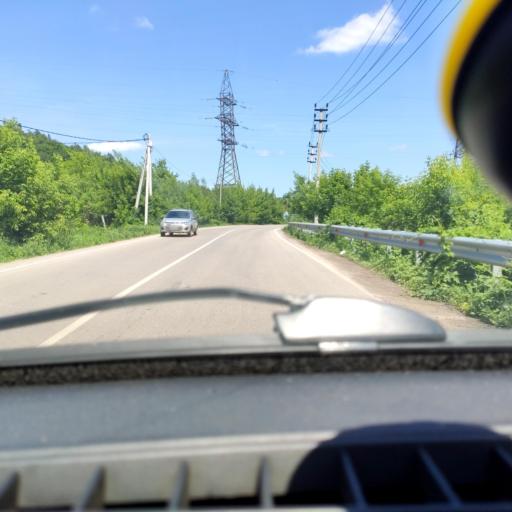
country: RU
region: Samara
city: Zhigulevsk
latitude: 53.3857
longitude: 49.5056
